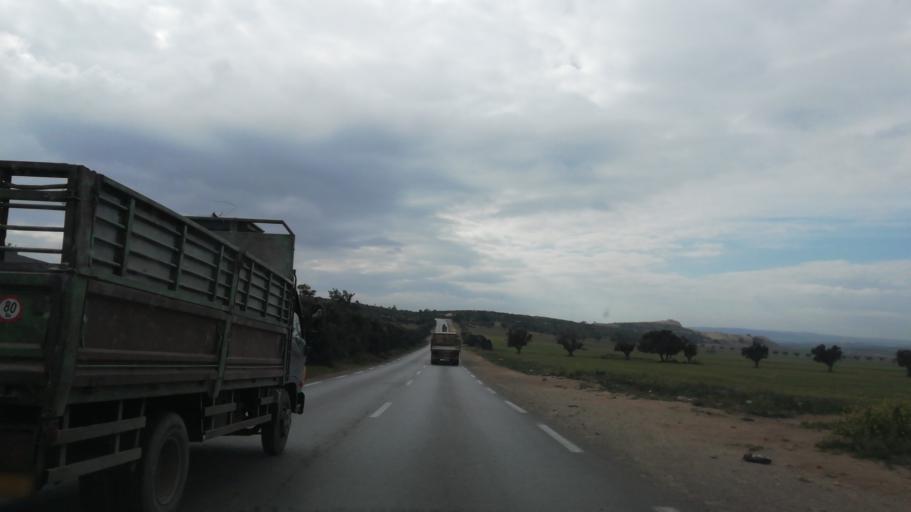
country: DZ
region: Oran
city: Ain el Bya
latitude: 35.7246
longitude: -0.3560
